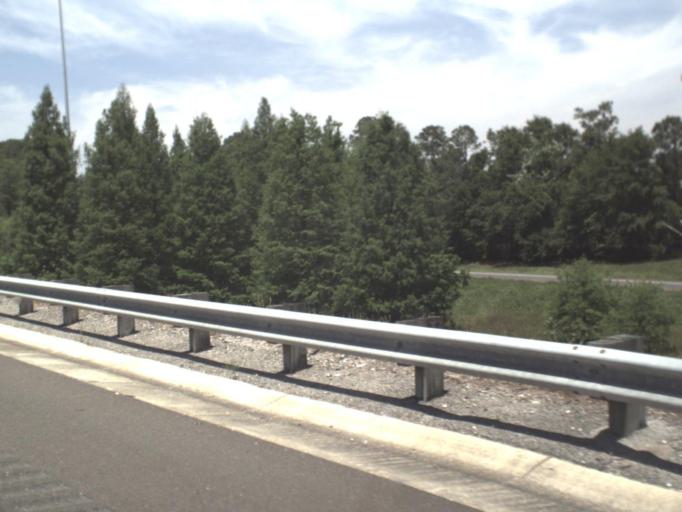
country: US
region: Florida
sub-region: Duval County
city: Jacksonville
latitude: 30.4470
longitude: -81.6110
